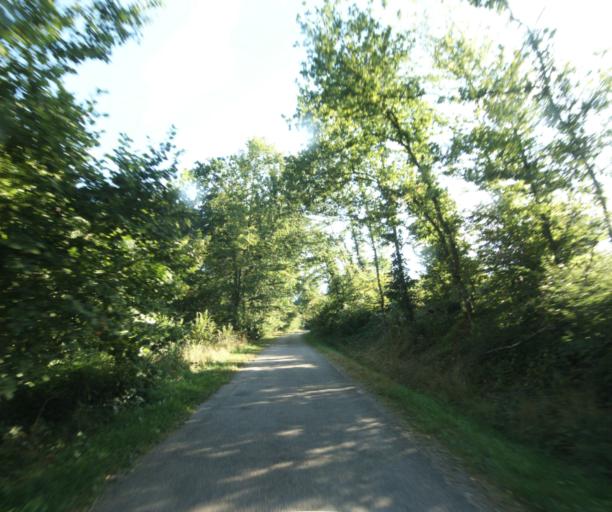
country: FR
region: Lorraine
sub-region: Departement des Vosges
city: Urimenil
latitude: 48.1266
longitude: 6.4255
